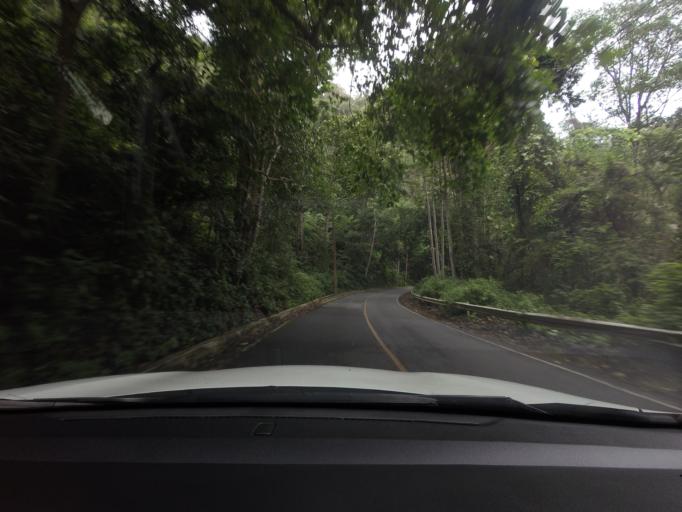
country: TH
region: Nakhon Ratchasima
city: Pak Chong
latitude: 14.4797
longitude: 101.3851
